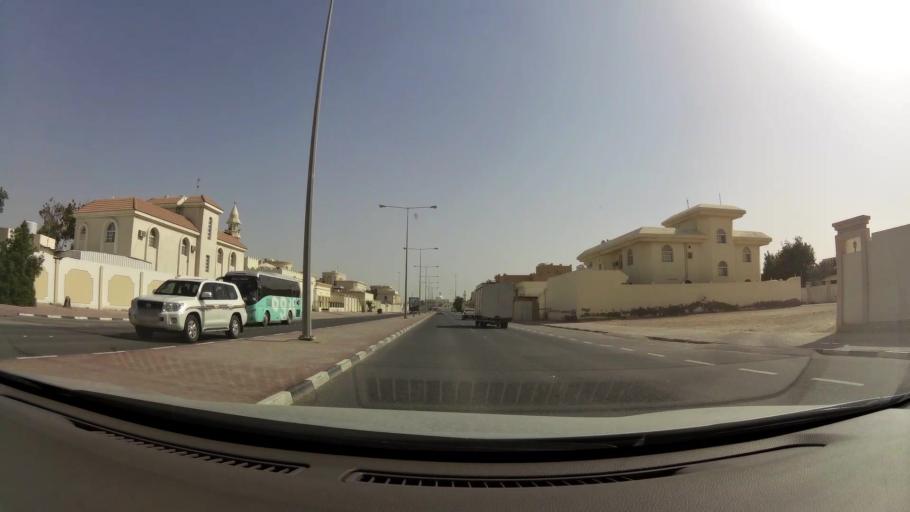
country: QA
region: Baladiyat Umm Salal
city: Umm Salal Muhammad
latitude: 25.3676
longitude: 51.4354
